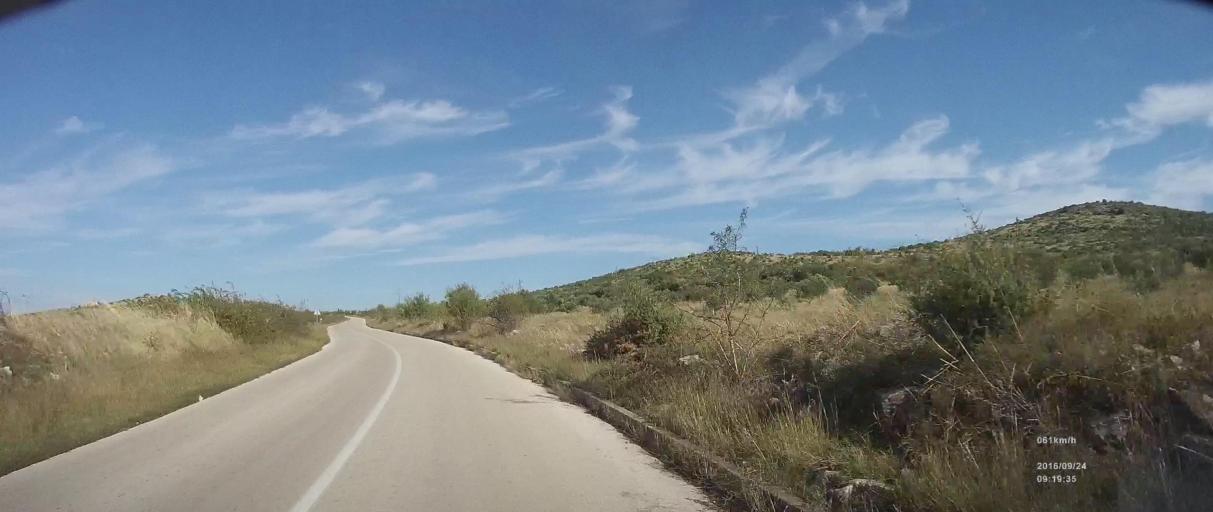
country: HR
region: Zadarska
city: Polaca
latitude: 44.0629
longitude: 15.5036
